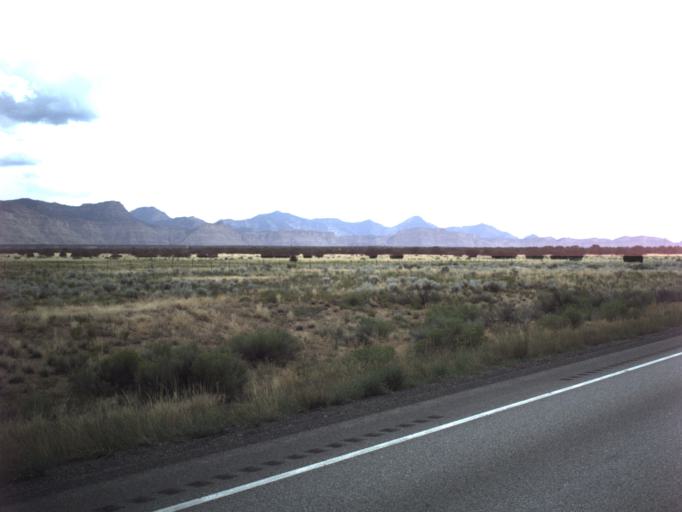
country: US
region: Utah
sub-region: Carbon County
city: East Carbon City
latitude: 39.4265
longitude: -110.4474
